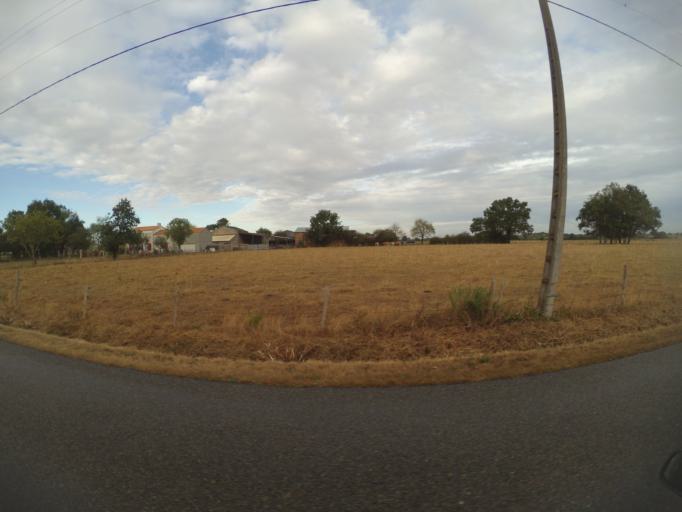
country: FR
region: Pays de la Loire
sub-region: Departement de la Loire-Atlantique
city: La Planche
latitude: 47.0425
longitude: -1.4152
